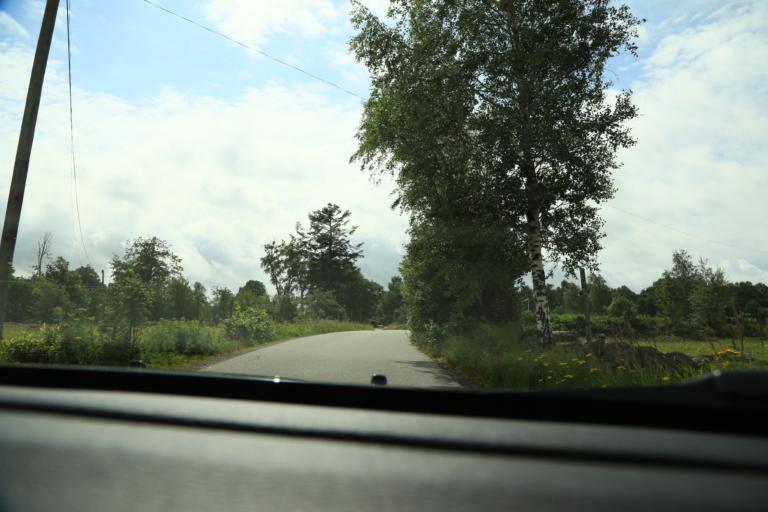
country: SE
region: Halland
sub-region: Varbergs Kommun
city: Traslovslage
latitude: 57.1176
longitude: 12.3084
